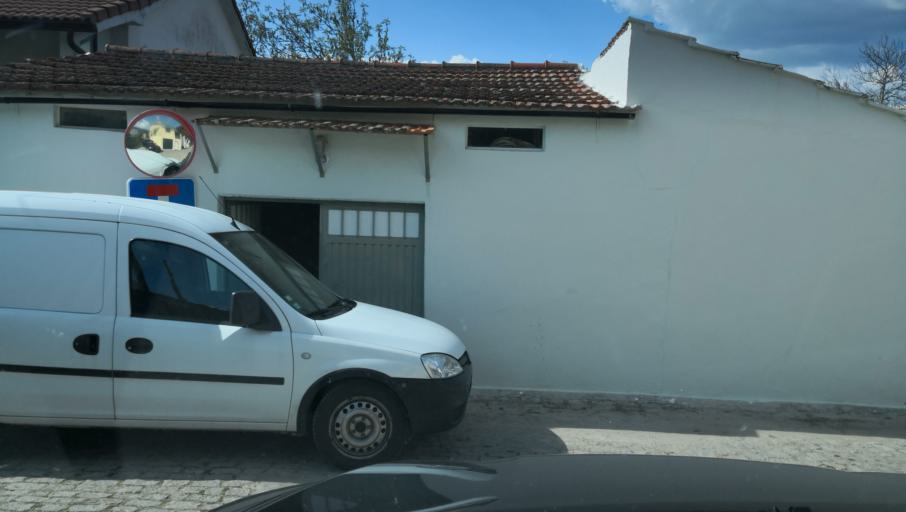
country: PT
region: Vila Real
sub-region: Sabrosa
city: Vilela
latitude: 41.2387
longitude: -7.6766
